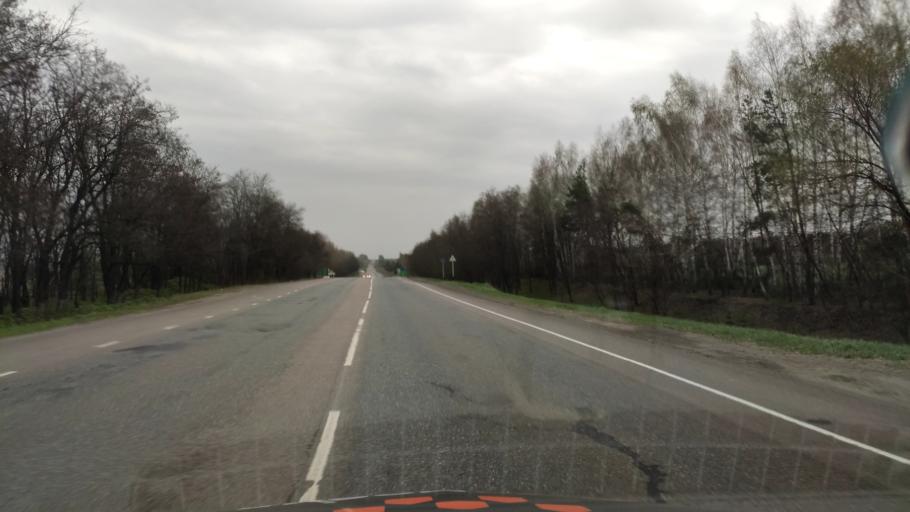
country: RU
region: Belgorod
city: Staryy Oskol
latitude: 51.4335
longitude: 37.9018
